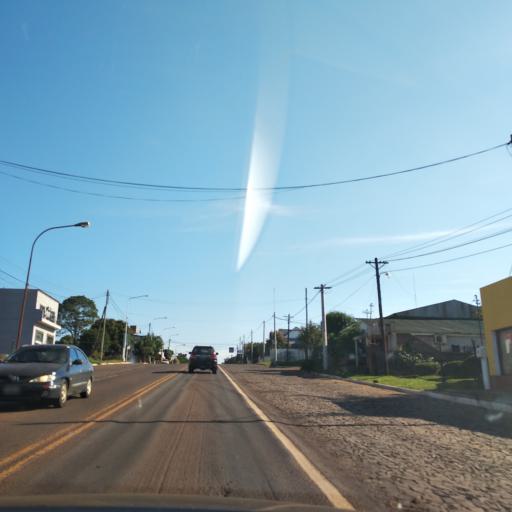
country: AR
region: Misiones
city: Gobernador Roca
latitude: -27.1842
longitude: -55.4623
